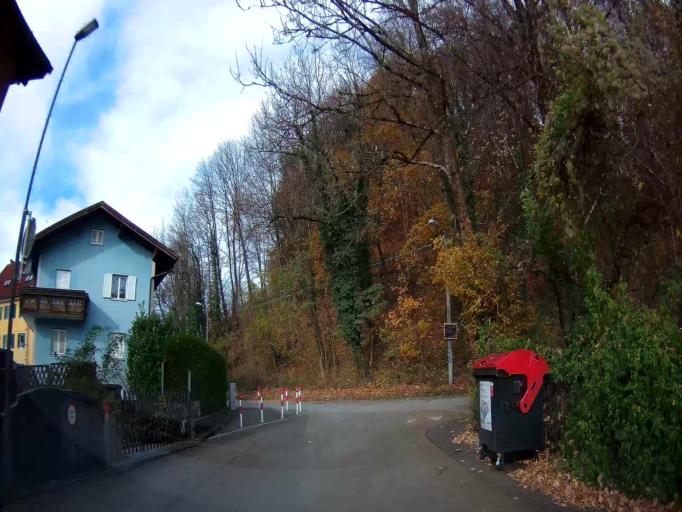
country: AT
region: Salzburg
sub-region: Salzburg Stadt
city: Salzburg
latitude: 47.8076
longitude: 13.0737
